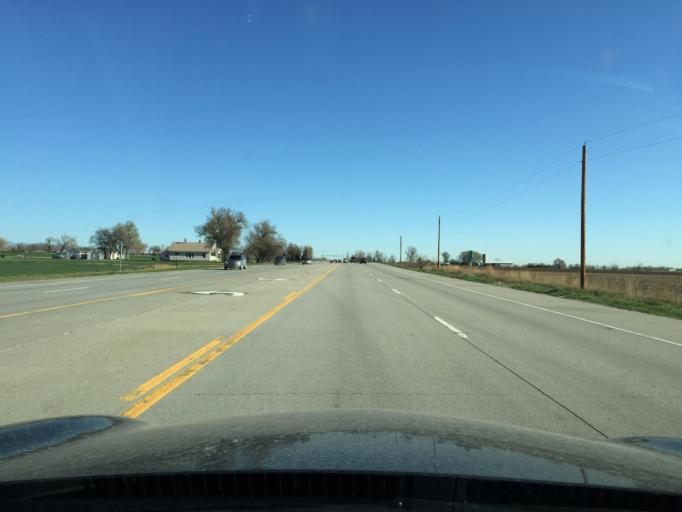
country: US
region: Colorado
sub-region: Boulder County
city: Erie
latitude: 40.0807
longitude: -105.1026
